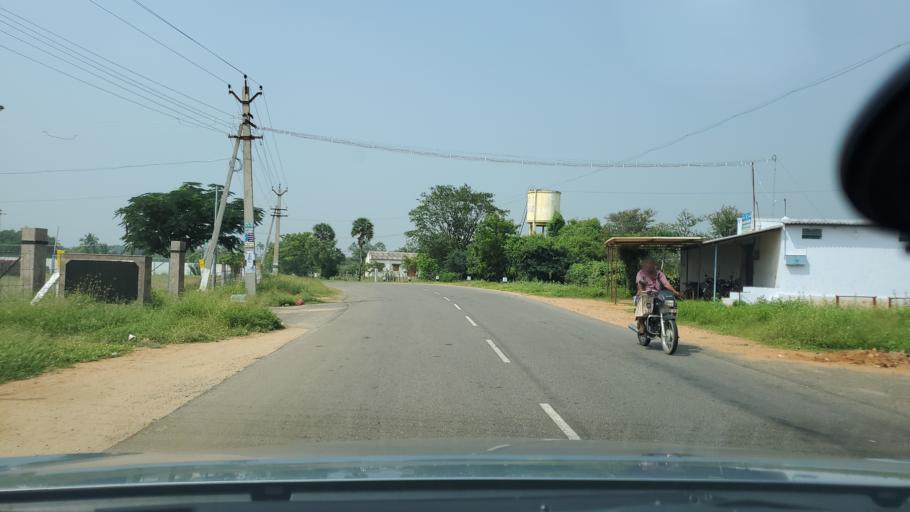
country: IN
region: Tamil Nadu
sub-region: Erode
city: Chennimalai
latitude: 11.1919
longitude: 77.6224
